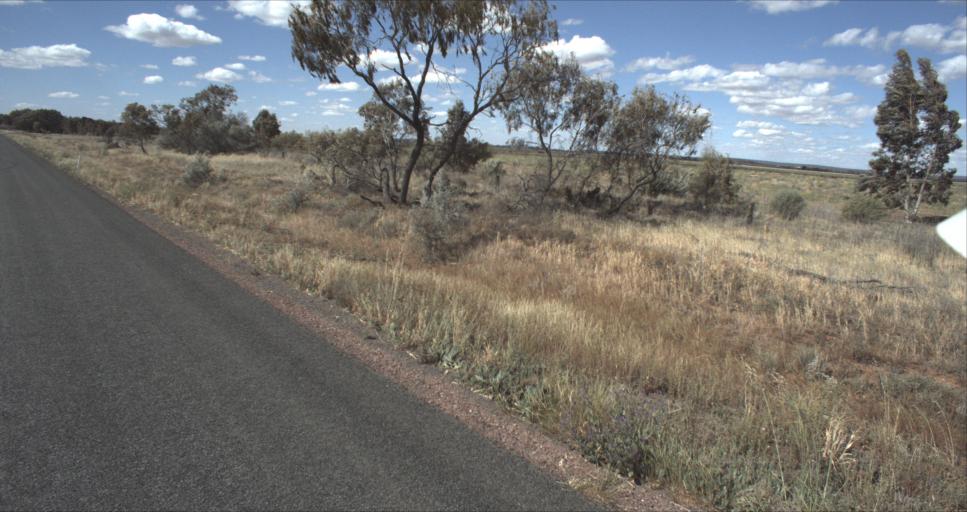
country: AU
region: New South Wales
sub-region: Leeton
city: Leeton
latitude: -34.4341
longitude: 146.2576
